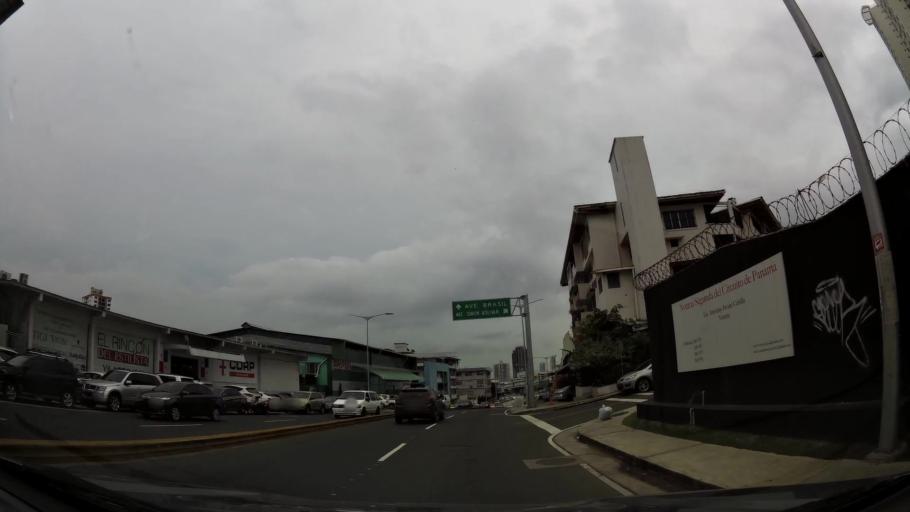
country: PA
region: Panama
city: Panama
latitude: 8.9961
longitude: -79.5306
